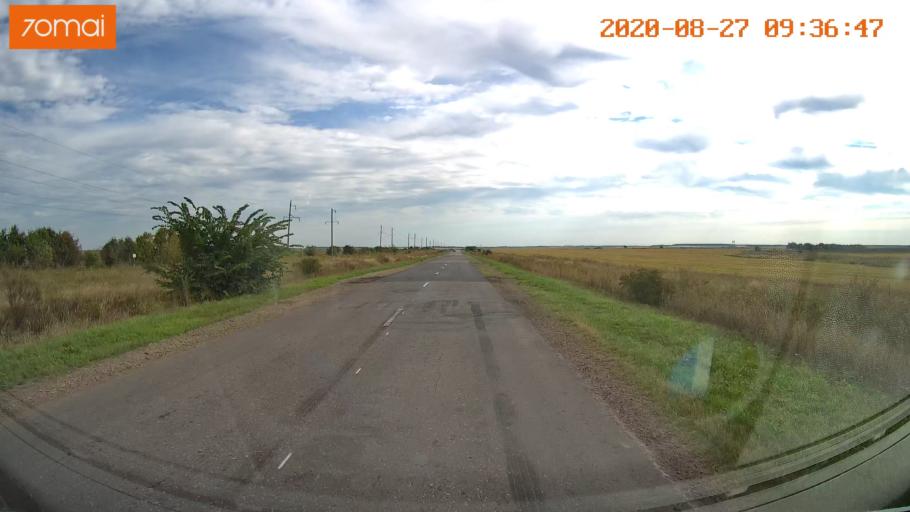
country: RU
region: Tula
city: Kazachka
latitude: 53.3659
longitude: 38.3485
